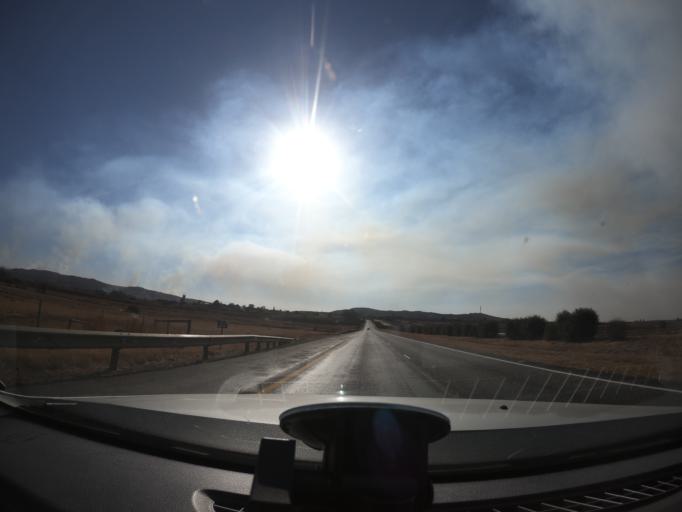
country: ZA
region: Gauteng
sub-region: Sedibeng District Municipality
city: Heidelberg
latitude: -26.5031
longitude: 28.3828
